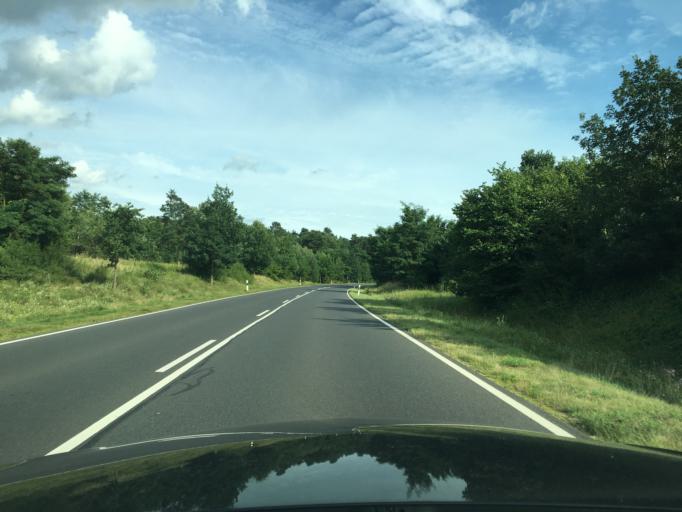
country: DE
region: Mecklenburg-Vorpommern
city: Neustrelitz
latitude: 53.3775
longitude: 13.0675
